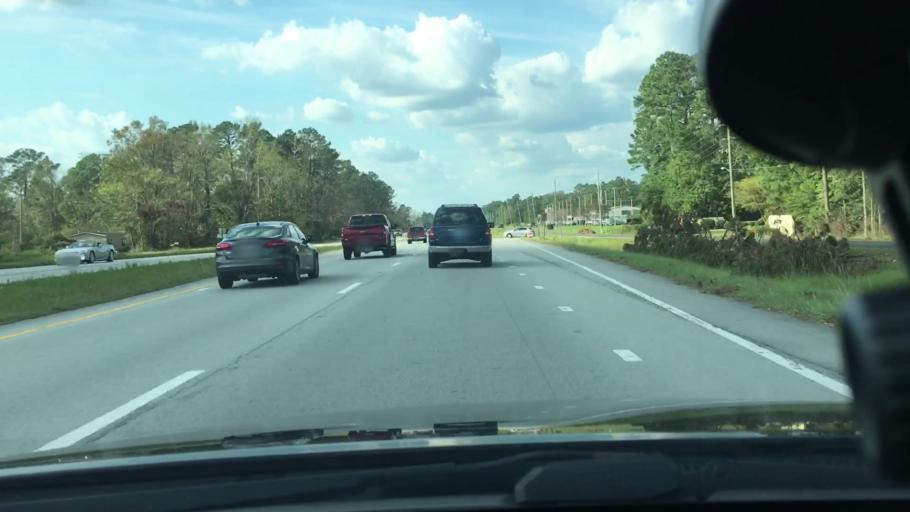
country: US
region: North Carolina
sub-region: Craven County
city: Neuse Forest
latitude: 35.0017
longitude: -76.9873
